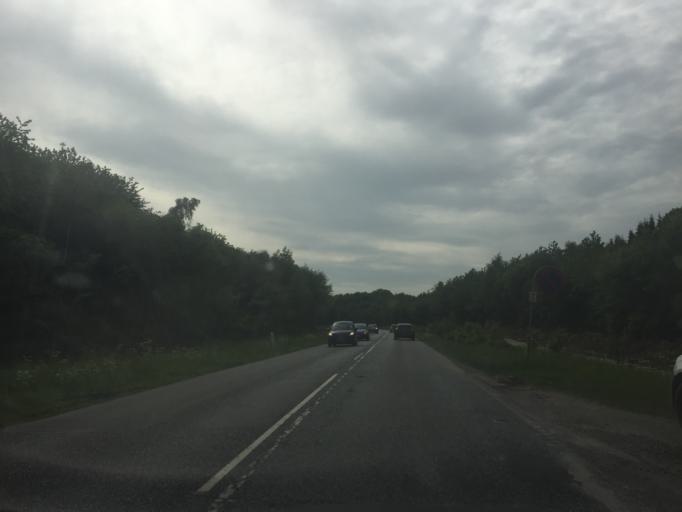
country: DK
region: Capital Region
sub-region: Albertslund Kommune
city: Albertslund
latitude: 55.6829
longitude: 12.3602
